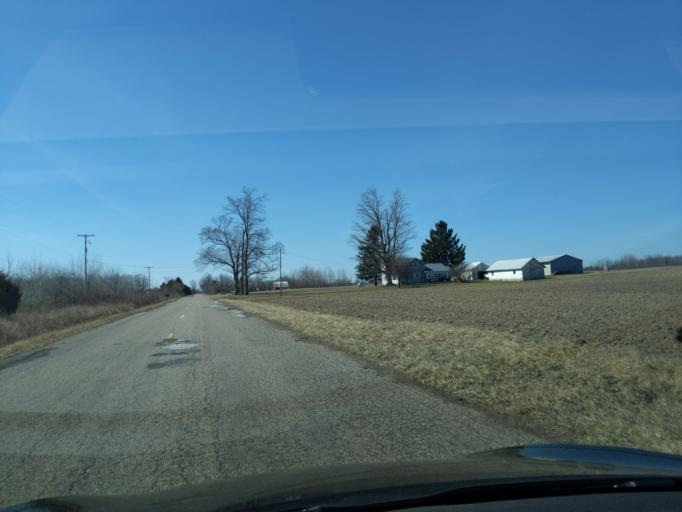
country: US
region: Michigan
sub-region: Ionia County
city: Portland
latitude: 42.7267
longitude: -84.9620
